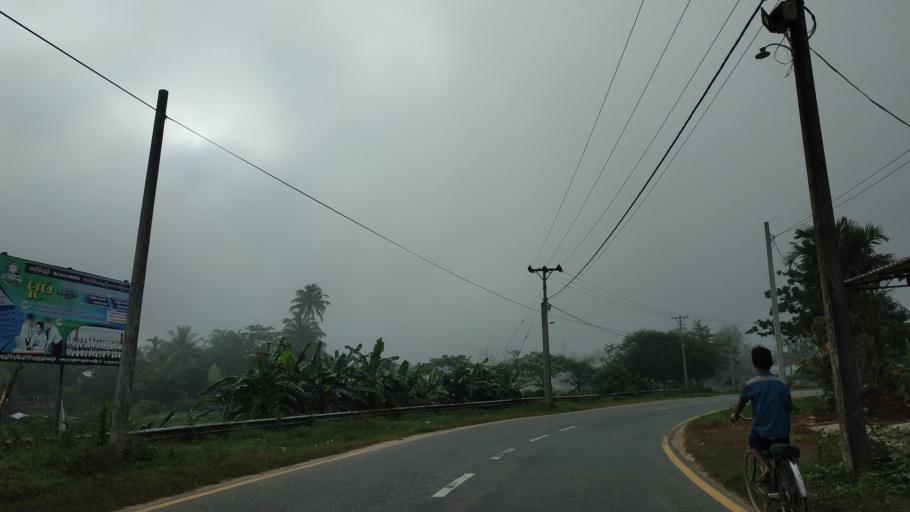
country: MM
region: Tanintharyi
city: Dawei
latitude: 14.1123
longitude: 98.2045
